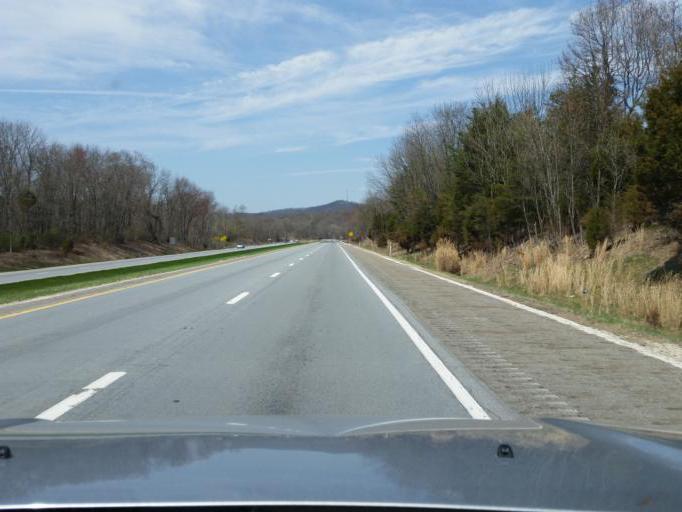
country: US
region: Pennsylvania
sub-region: Perry County
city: Newport
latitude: 40.5345
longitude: -77.1402
